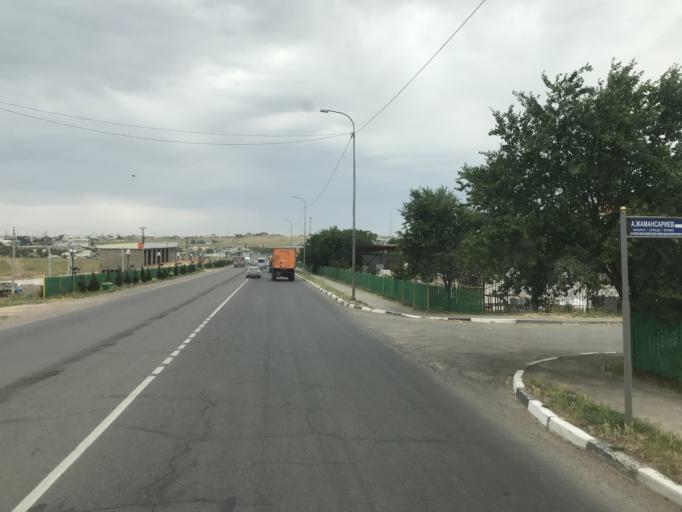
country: KZ
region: Ongtustik Qazaqstan
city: Saryaghash
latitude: 41.4729
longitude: 69.1902
